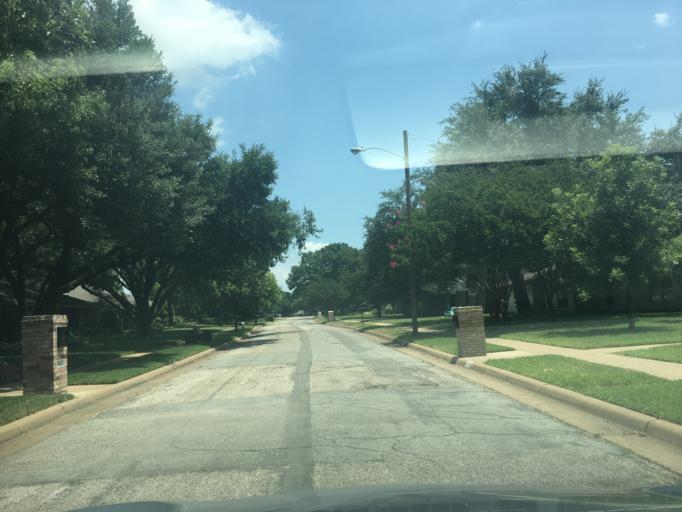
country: US
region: Texas
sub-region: Dallas County
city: Addison
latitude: 32.9148
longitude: -96.8406
